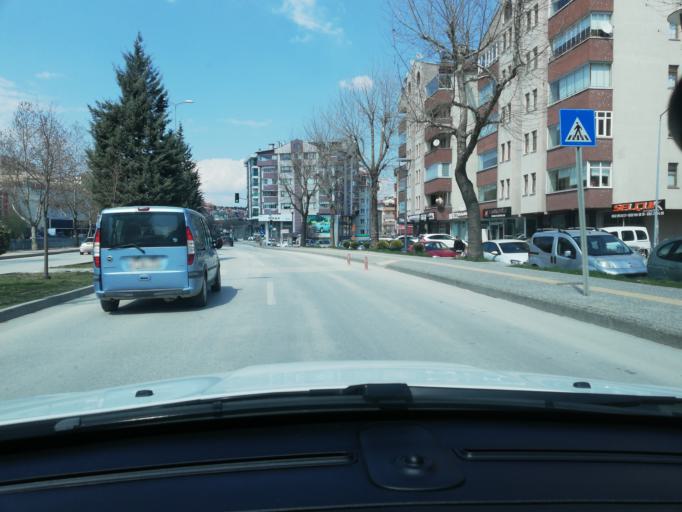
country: TR
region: Kastamonu
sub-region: Cide
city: Kastamonu
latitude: 41.3957
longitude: 33.7821
